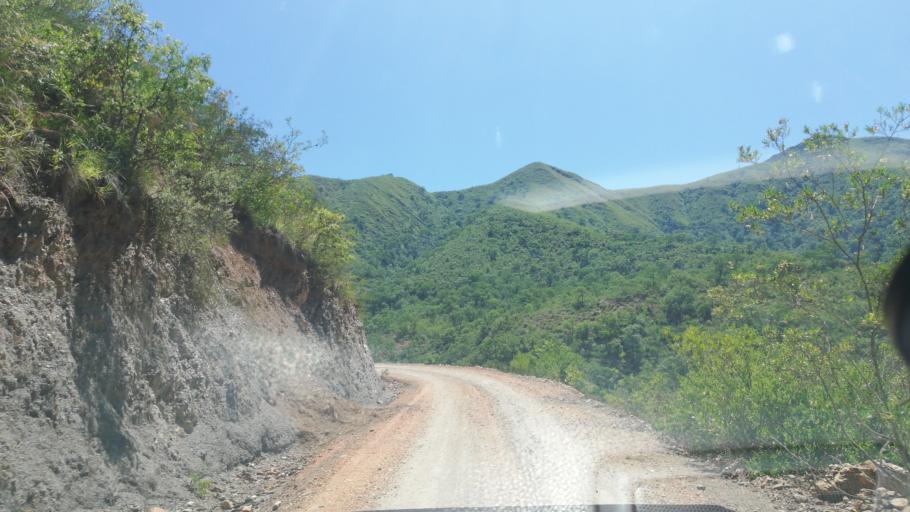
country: BO
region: Cochabamba
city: Mizque
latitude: -17.8762
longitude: -65.2923
